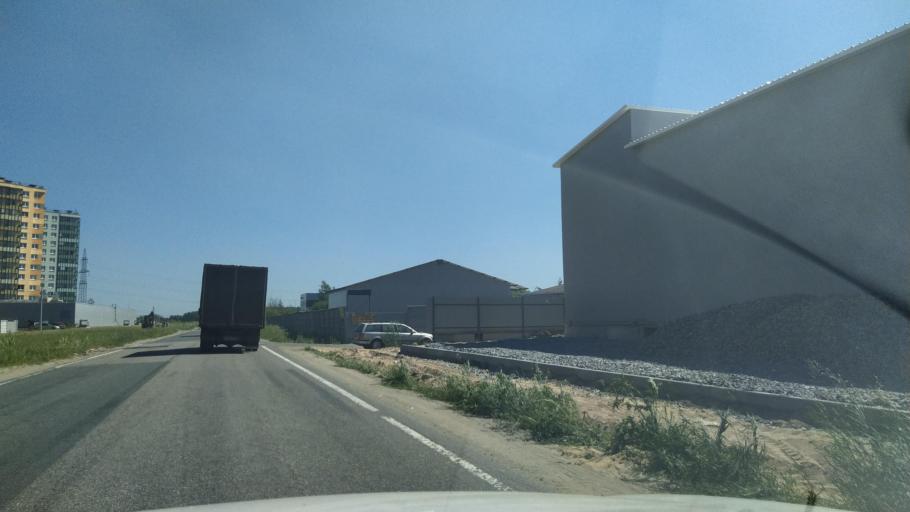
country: RU
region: St.-Petersburg
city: Krasnogvargeisky
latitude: 60.0013
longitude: 30.4493
